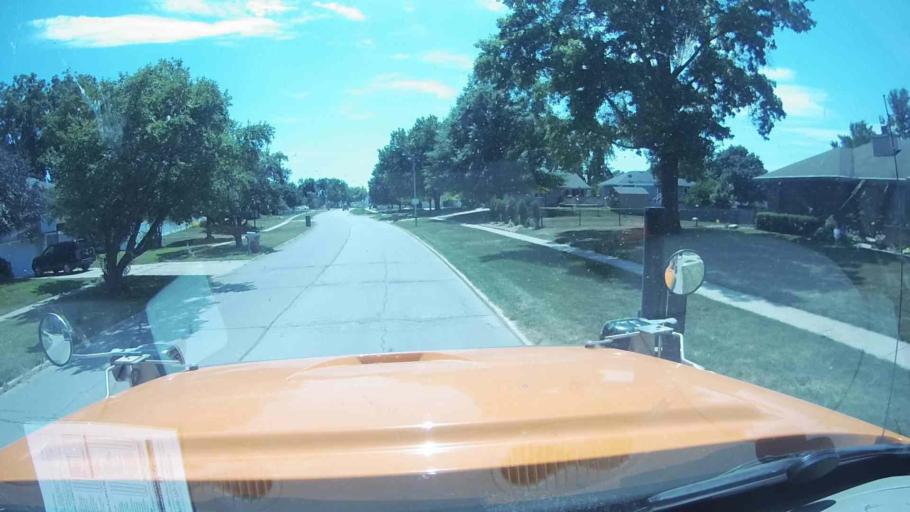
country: US
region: Iowa
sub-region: Polk County
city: Altoona
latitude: 41.6574
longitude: -93.4701
